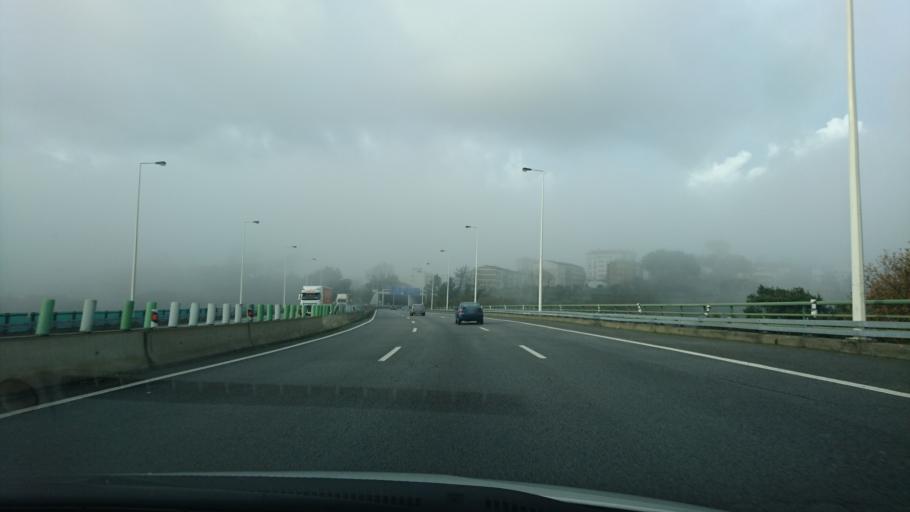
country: PT
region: Porto
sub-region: Gondomar
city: Rio Tinto
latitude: 41.1589
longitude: -8.5636
